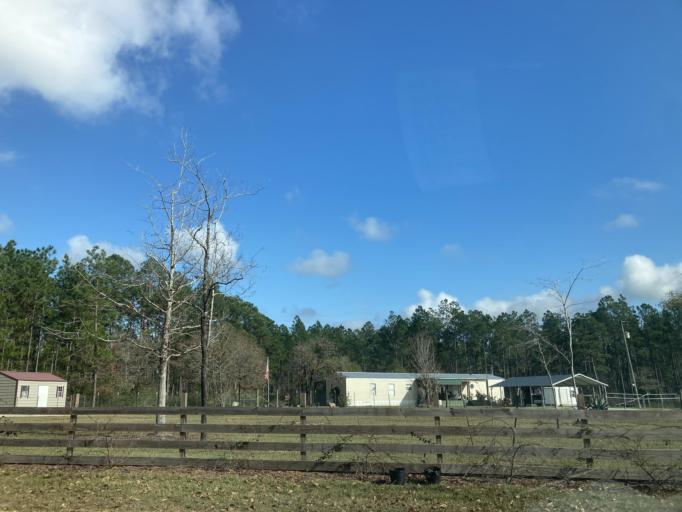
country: US
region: Mississippi
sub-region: Harrison County
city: Saucier
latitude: 30.6986
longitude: -89.2068
